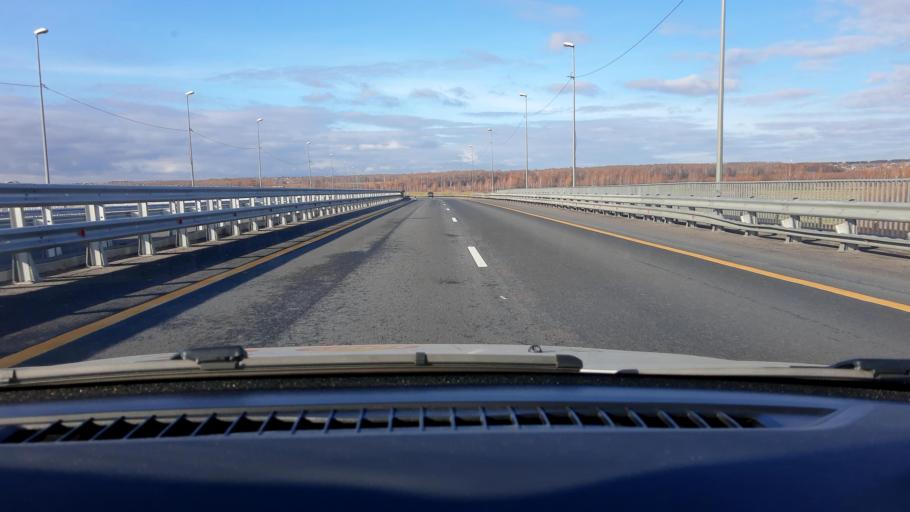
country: RU
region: Nizjnij Novgorod
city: Burevestnik
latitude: 56.1221
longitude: 43.8082
